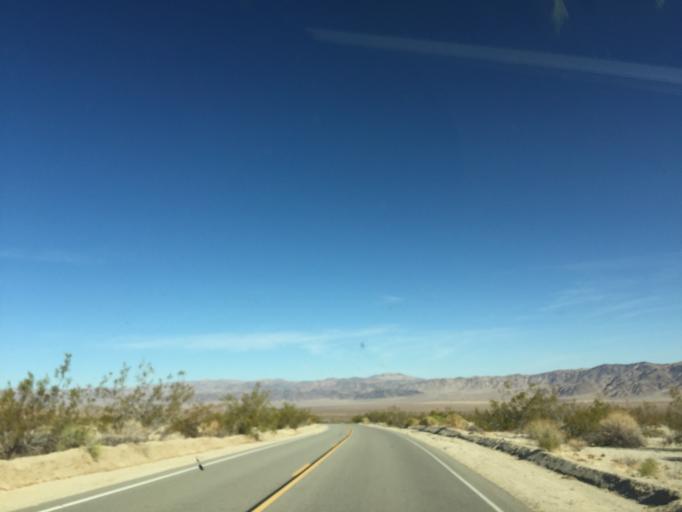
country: US
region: California
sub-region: San Bernardino County
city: Twentynine Palms
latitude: 33.8628
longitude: -115.7956
